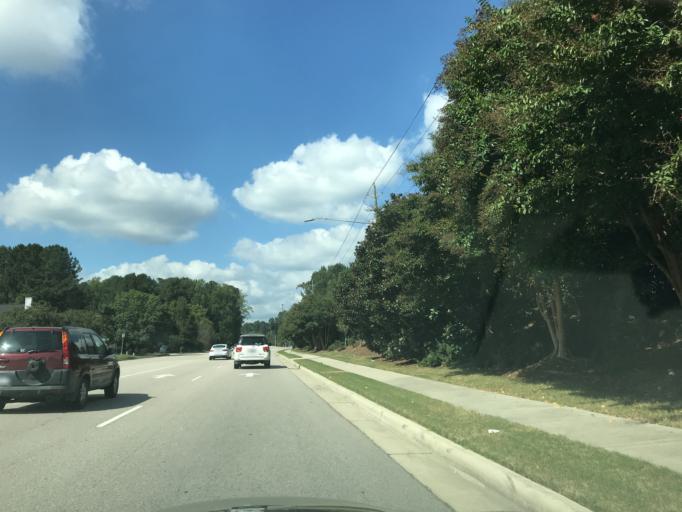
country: US
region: North Carolina
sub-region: Wake County
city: Wake Forest
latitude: 35.8879
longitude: -78.5551
